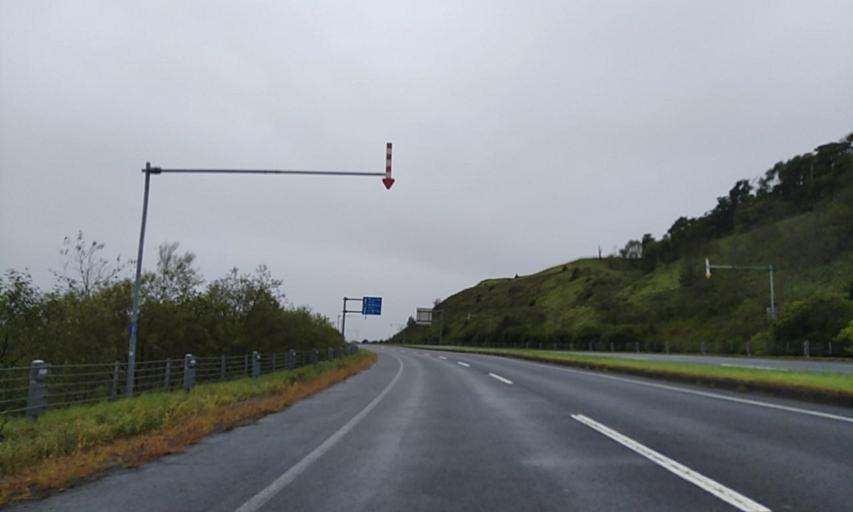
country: JP
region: Hokkaido
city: Kushiro
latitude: 43.0183
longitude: 144.2571
